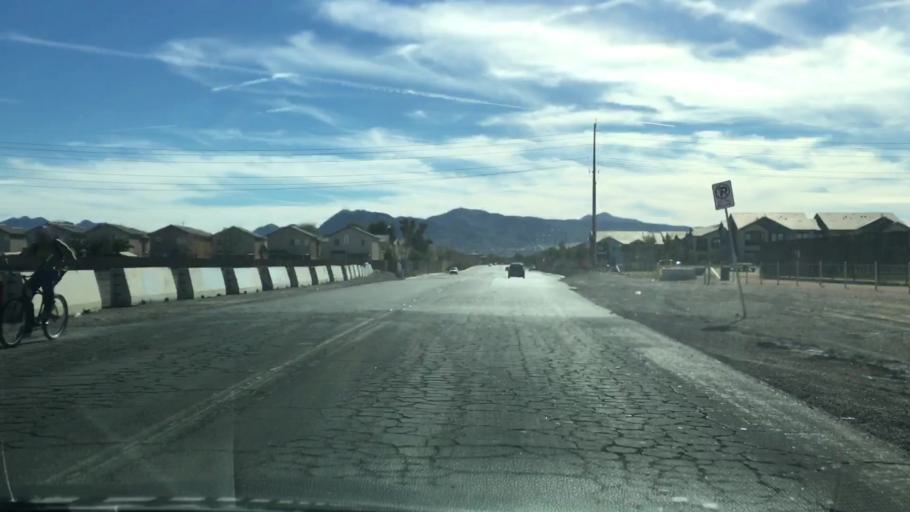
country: US
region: Nevada
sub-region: Clark County
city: Henderson
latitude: 36.0831
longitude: -115.0205
